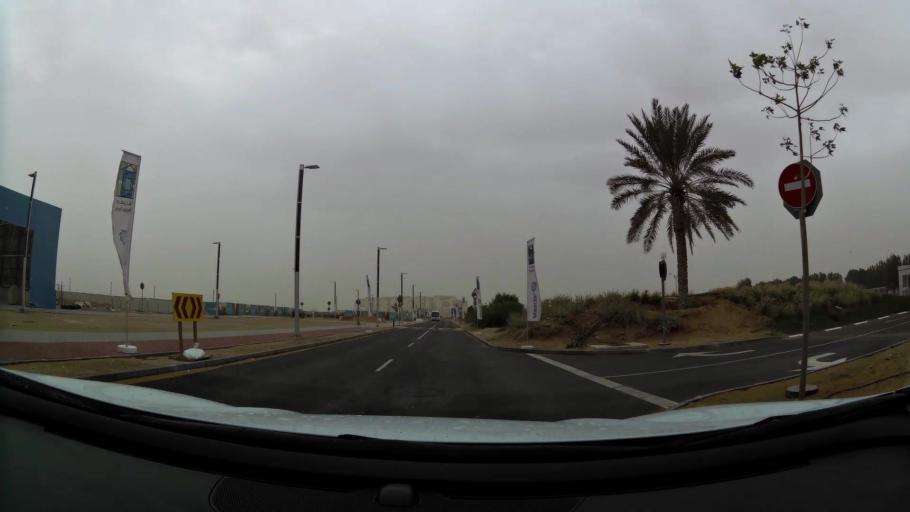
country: AE
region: Abu Dhabi
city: Abu Dhabi
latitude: 24.4370
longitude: 54.6193
